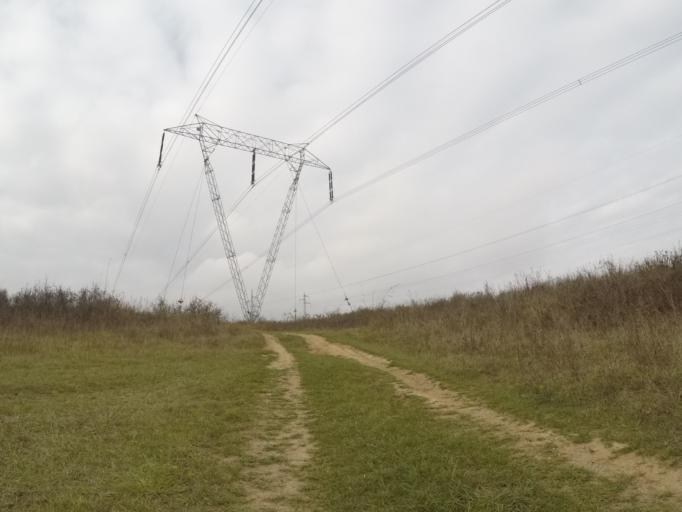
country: SK
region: Presovsky
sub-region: Okres Presov
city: Presov
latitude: 48.9047
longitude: 21.1794
